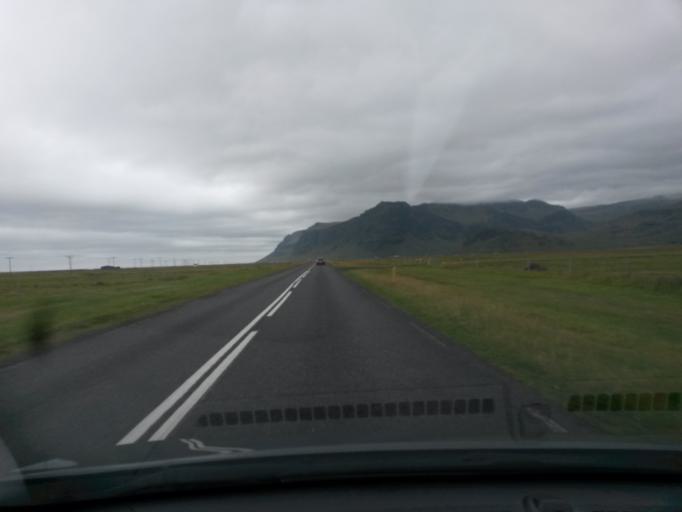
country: IS
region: South
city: Vestmannaeyjar
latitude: 63.5235
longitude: -19.5811
